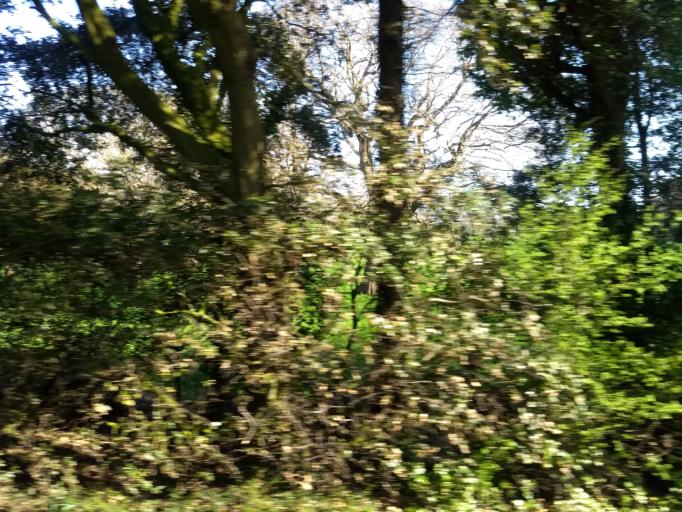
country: GB
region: England
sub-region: Isle of Wight
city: Seaview
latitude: 50.7192
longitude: -1.1312
